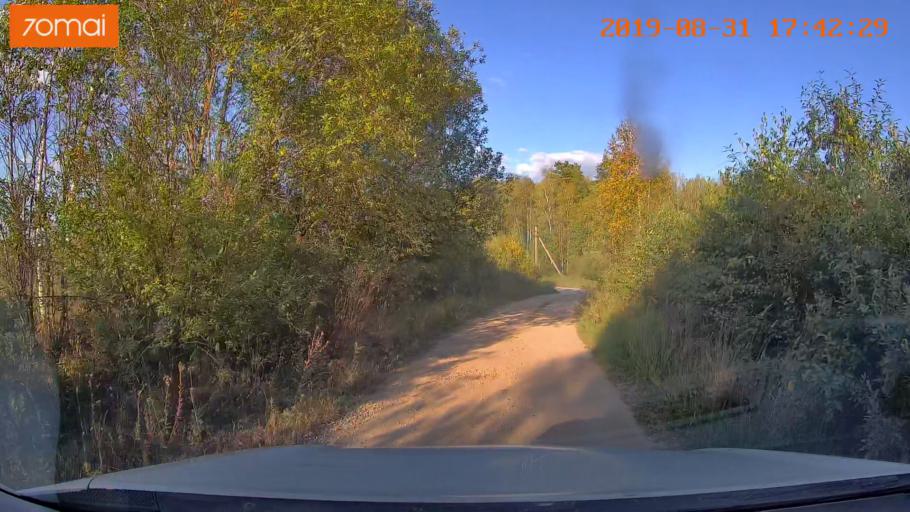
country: RU
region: Kaluga
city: Detchino
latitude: 54.8226
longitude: 36.3695
